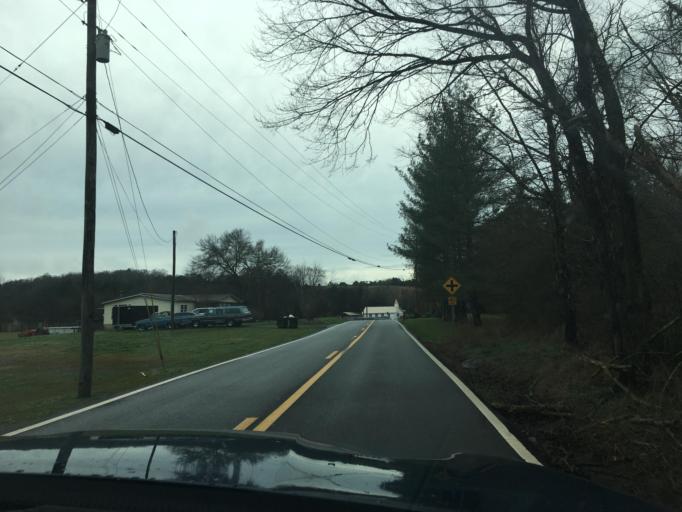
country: US
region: Tennessee
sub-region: McMinn County
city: Englewood
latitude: 35.4091
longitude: -84.4587
